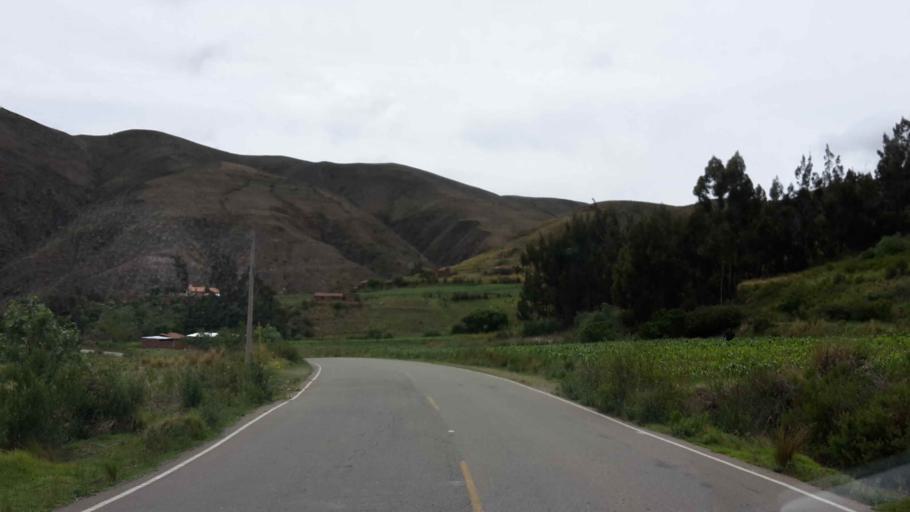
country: BO
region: Cochabamba
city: Colomi
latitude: -17.4090
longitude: -65.7800
